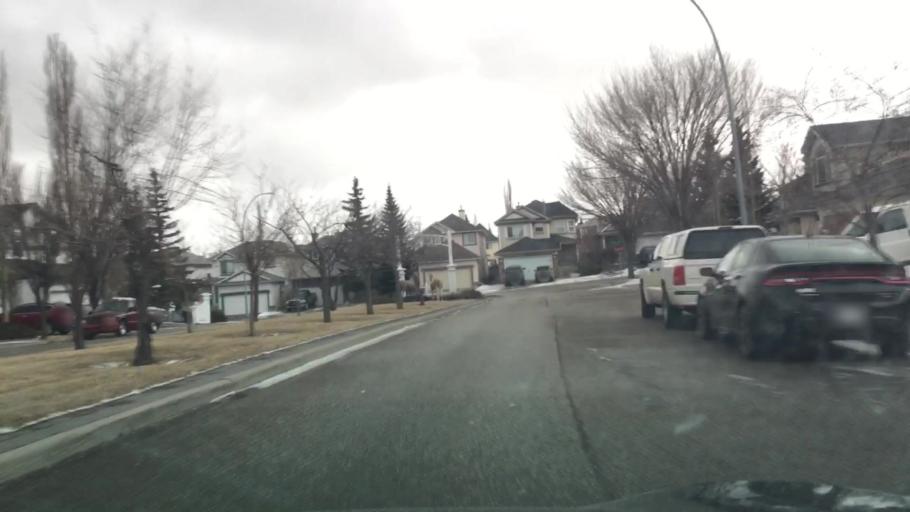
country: CA
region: Alberta
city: Calgary
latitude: 51.1474
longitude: -114.1189
